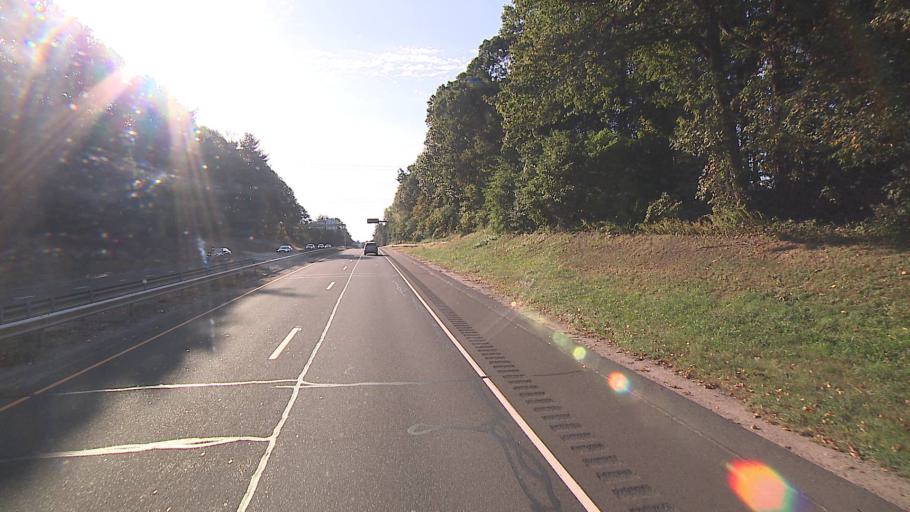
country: US
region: Connecticut
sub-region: New Haven County
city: City of Milford (balance)
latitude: 41.2428
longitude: -73.0810
